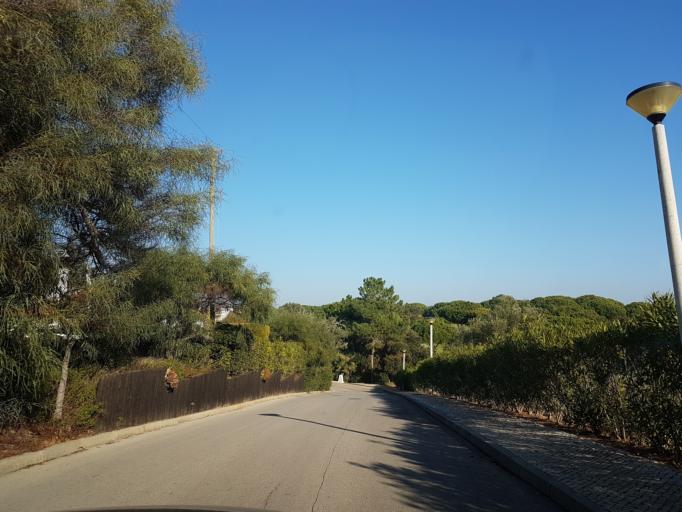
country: PT
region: Faro
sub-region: Albufeira
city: Albufeira
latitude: 37.0965
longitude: -8.2076
